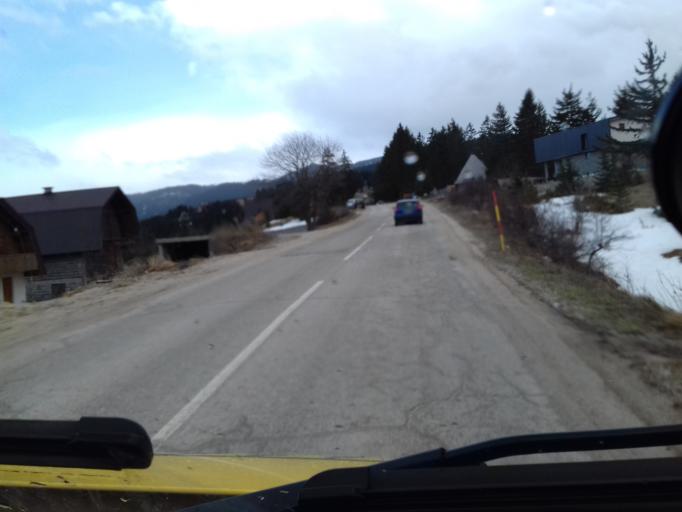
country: BA
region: Federation of Bosnia and Herzegovina
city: Turbe
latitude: 44.3152
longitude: 17.5542
